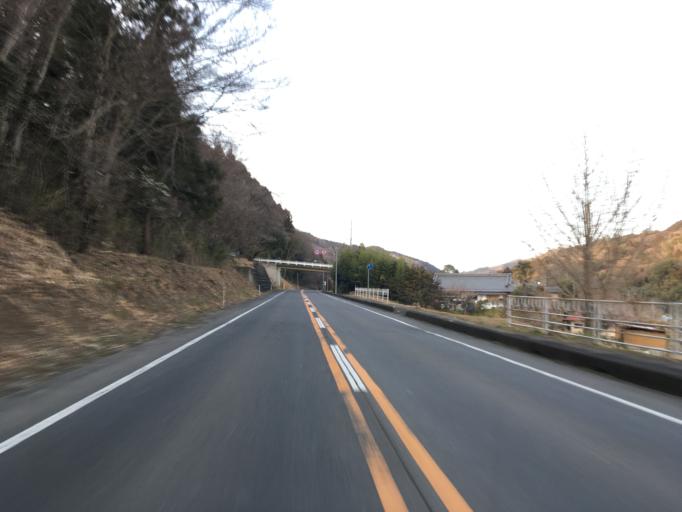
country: JP
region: Ibaraki
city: Daigo
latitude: 36.8237
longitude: 140.3790
